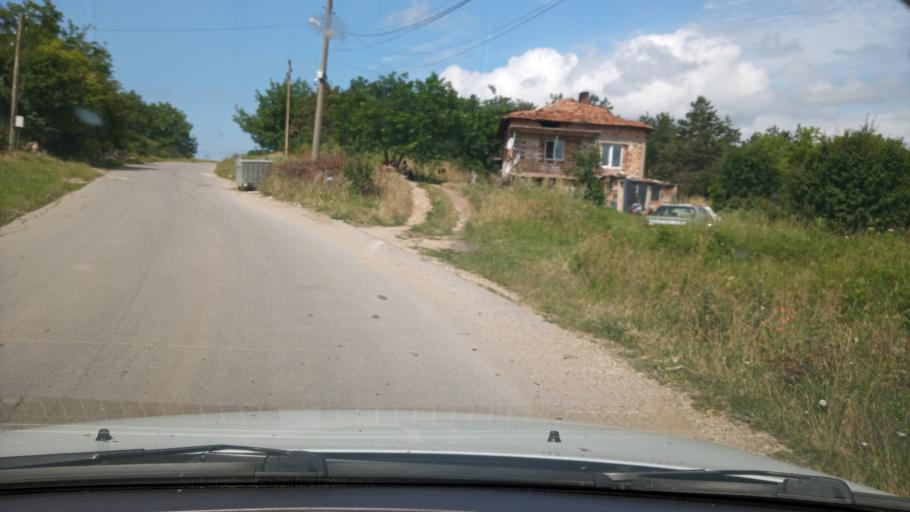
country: BG
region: Lovech
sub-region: Obshtina Lukovit
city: Lukovit
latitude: 43.2078
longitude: 24.1522
